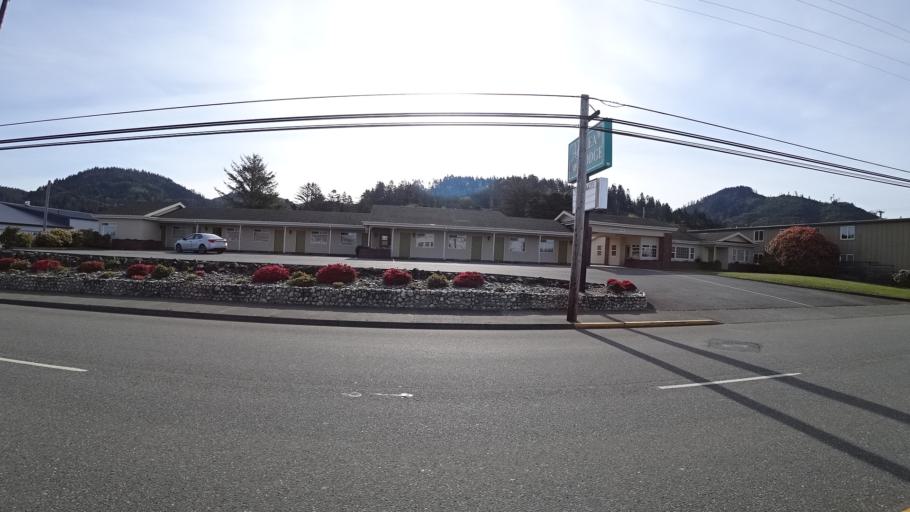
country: US
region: Oregon
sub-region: Curry County
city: Gold Beach
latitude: 42.4081
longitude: -124.4209
